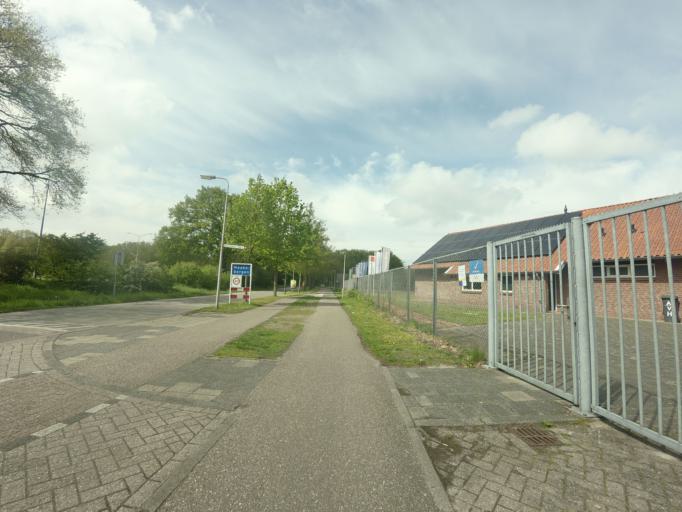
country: NL
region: Overijssel
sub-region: Gemeente Haaksbergen
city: Haaksbergen
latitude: 52.1436
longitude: 6.7278
